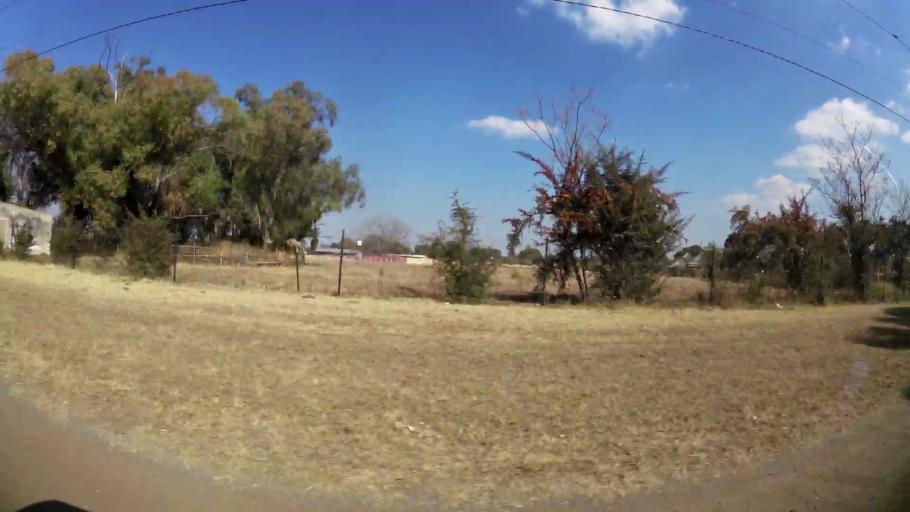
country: ZA
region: Gauteng
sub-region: Ekurhuleni Metropolitan Municipality
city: Benoni
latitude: -26.0992
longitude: 28.4107
